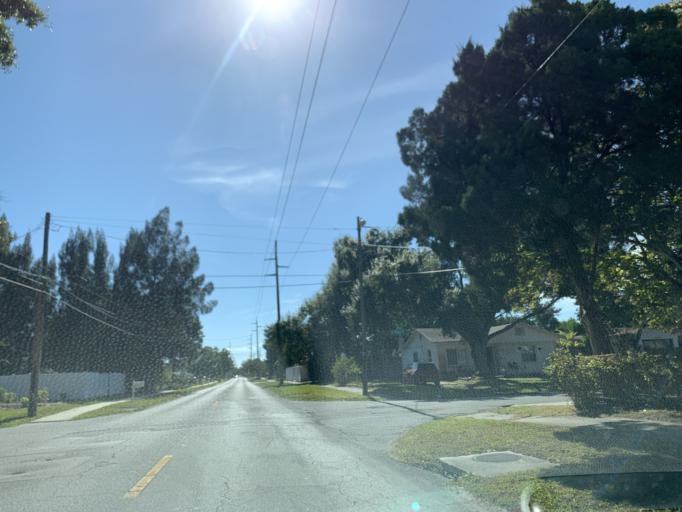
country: US
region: Florida
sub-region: Hillsborough County
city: Tampa
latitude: 27.8870
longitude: -82.5022
